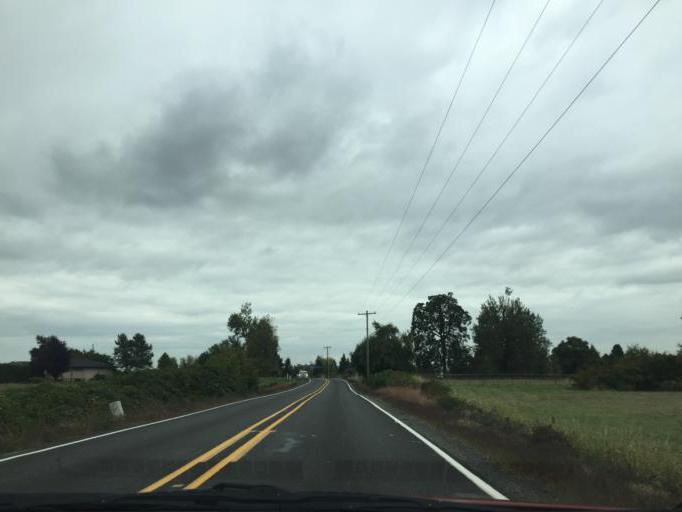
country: US
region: Oregon
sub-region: Washington County
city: Oak Hills
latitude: 45.6331
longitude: -122.7971
